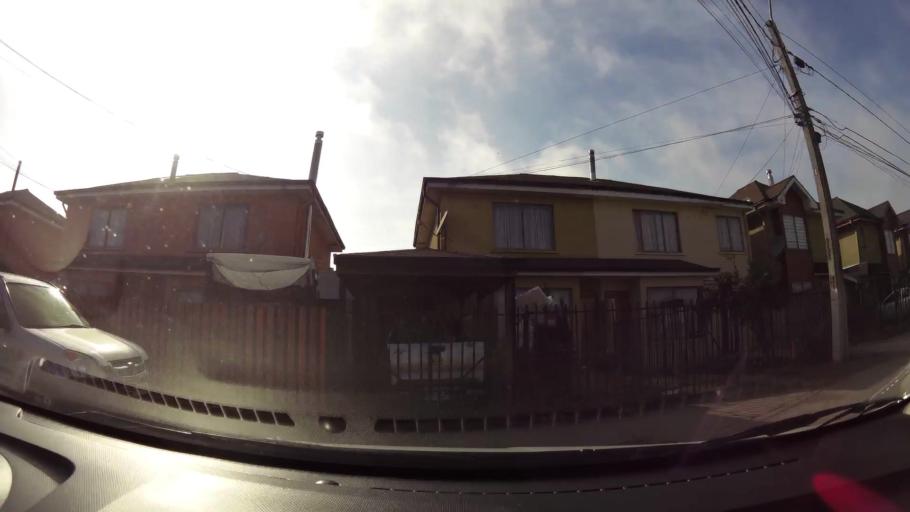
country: CL
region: Biobio
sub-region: Provincia de Concepcion
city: Concepcion
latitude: -36.7991
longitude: -73.1121
